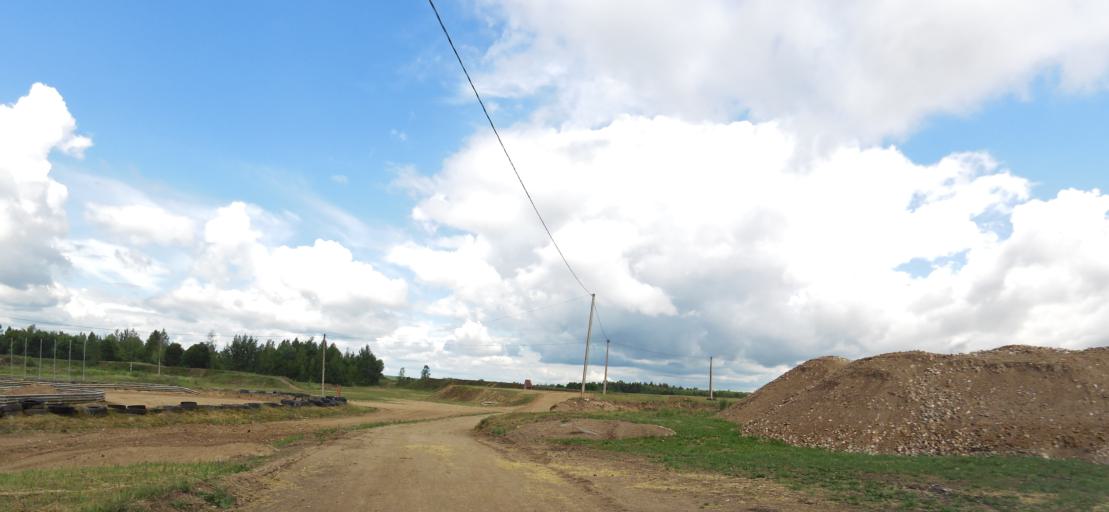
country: LT
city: Vabalninkas
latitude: 55.8880
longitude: 24.7754
